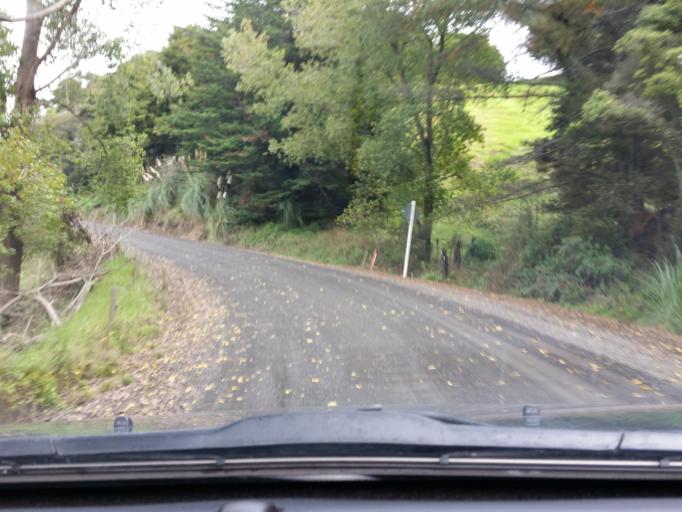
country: NZ
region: Northland
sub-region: Kaipara District
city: Dargaville
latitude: -35.8764
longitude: 174.0103
